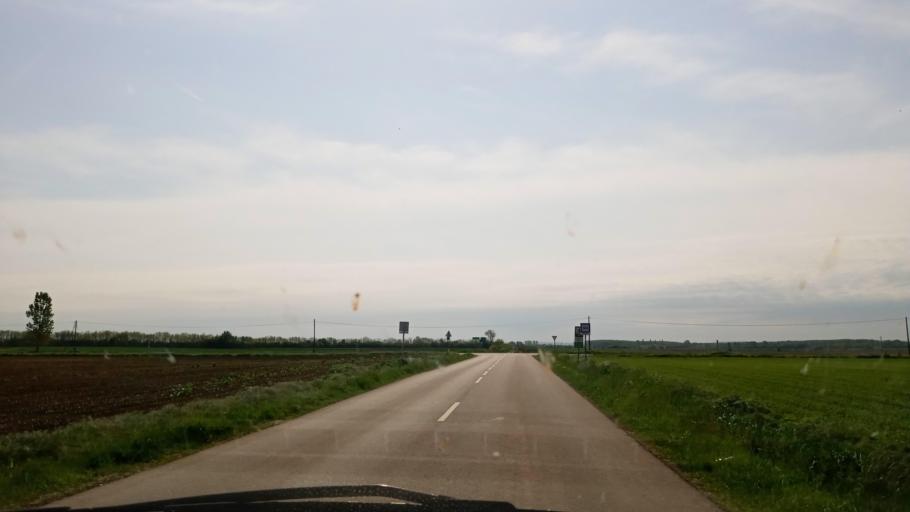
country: HU
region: Baranya
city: Lanycsok
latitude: 45.9312
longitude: 18.6081
